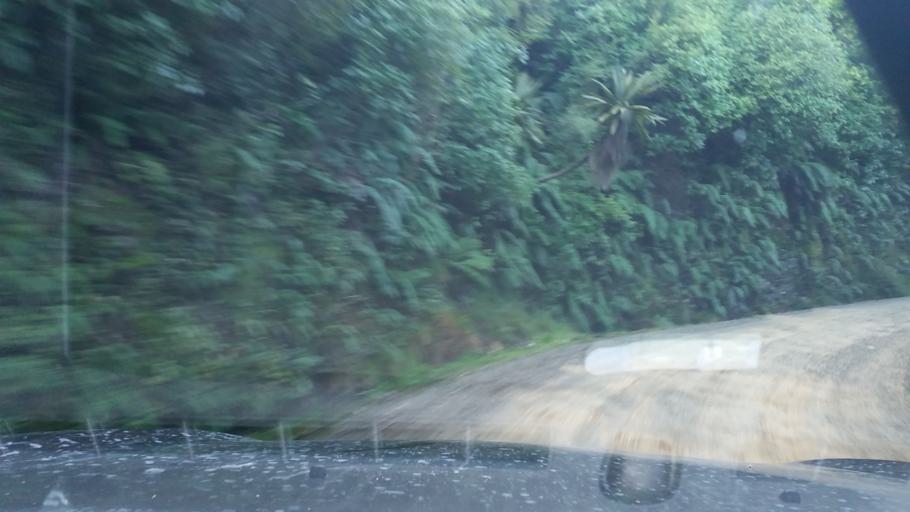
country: NZ
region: Marlborough
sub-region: Marlborough District
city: Picton
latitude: -41.0897
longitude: 174.1370
